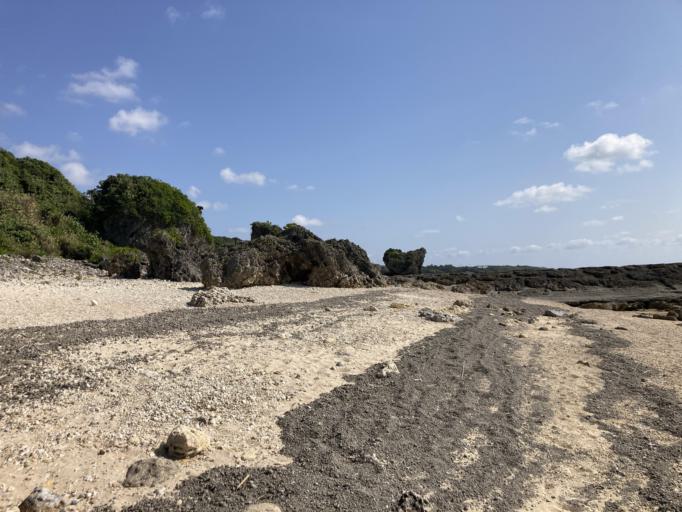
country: JP
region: Okinawa
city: Itoman
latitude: 26.1166
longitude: 127.7457
